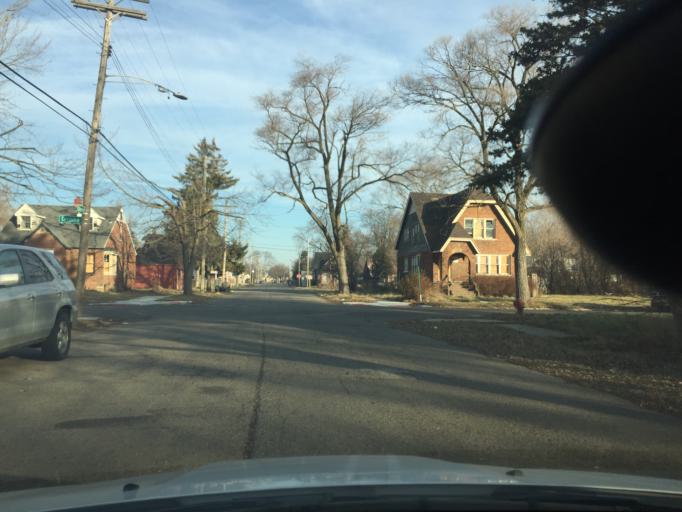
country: US
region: Michigan
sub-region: Macomb County
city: Eastpointe
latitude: 42.4415
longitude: -82.9688
